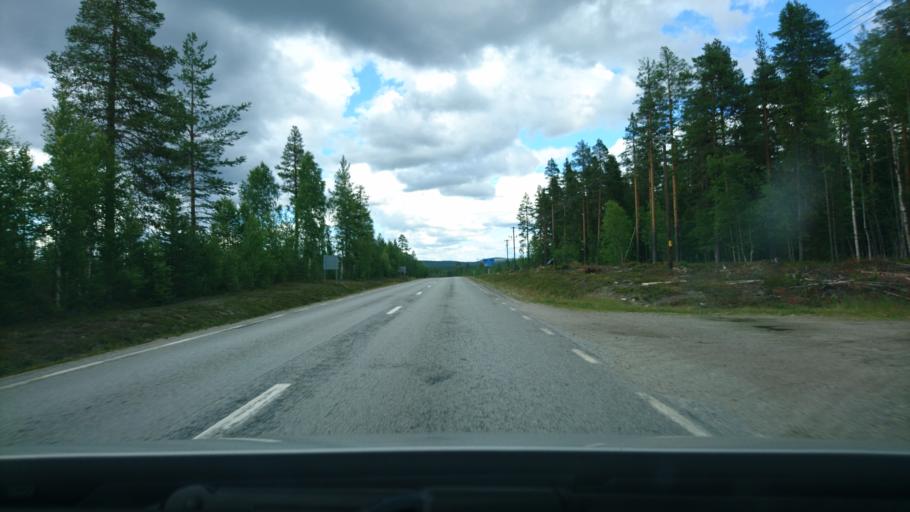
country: SE
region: Vaesterbotten
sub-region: Asele Kommun
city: Asele
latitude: 63.9153
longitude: 17.2335
